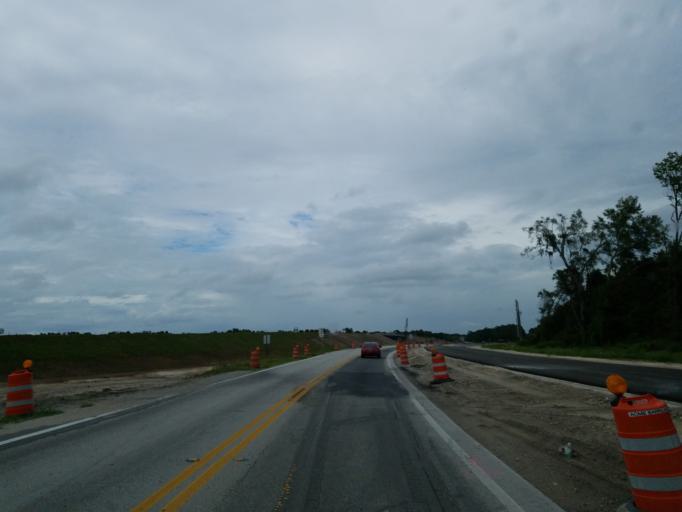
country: US
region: Florida
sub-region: Sumter County
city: Lake Panasoffkee
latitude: 28.7510
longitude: -82.1029
